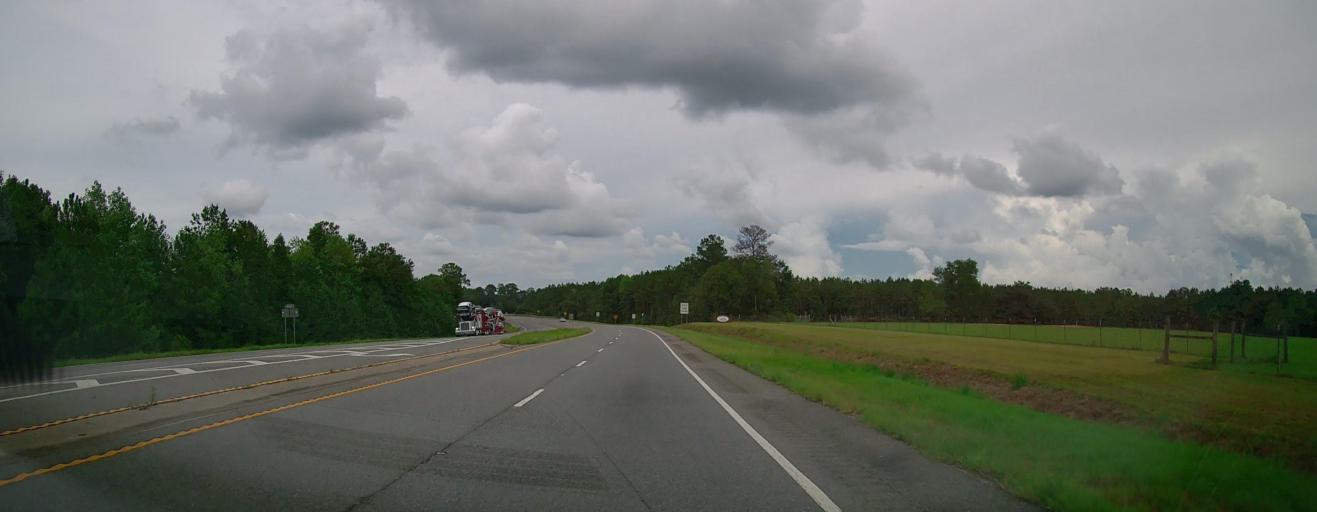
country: US
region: Georgia
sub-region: Wayne County
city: Jesup
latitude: 31.6679
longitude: -82.0455
